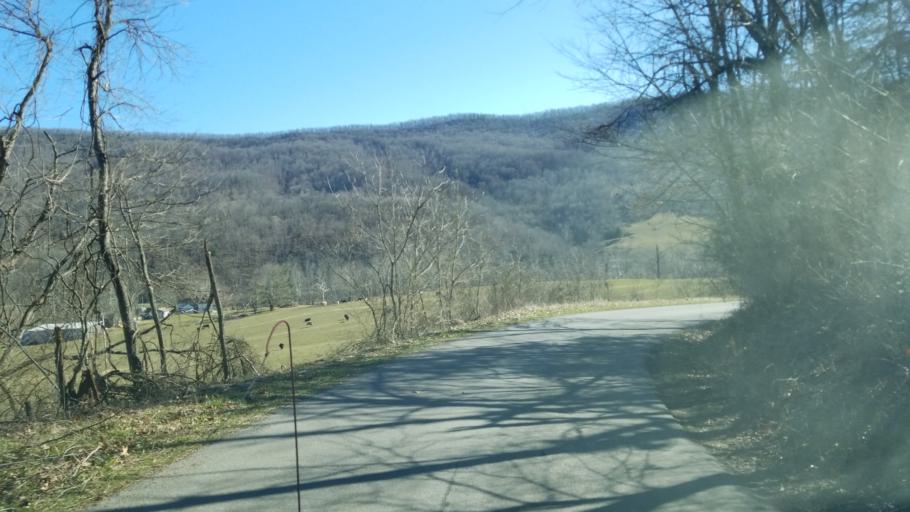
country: US
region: Virginia
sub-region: Pulaski County
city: Pulaski
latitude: 37.1638
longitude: -80.8585
